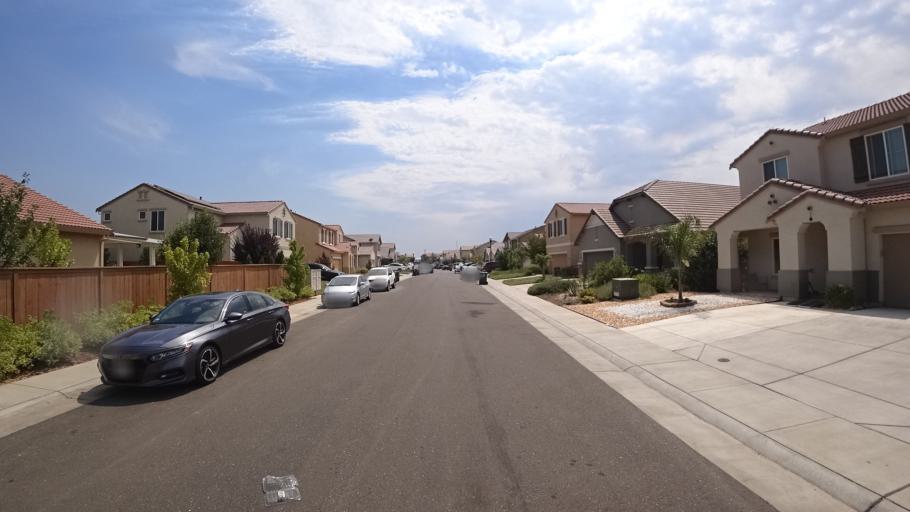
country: US
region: California
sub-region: Sacramento County
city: Laguna
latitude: 38.3936
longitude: -121.4148
